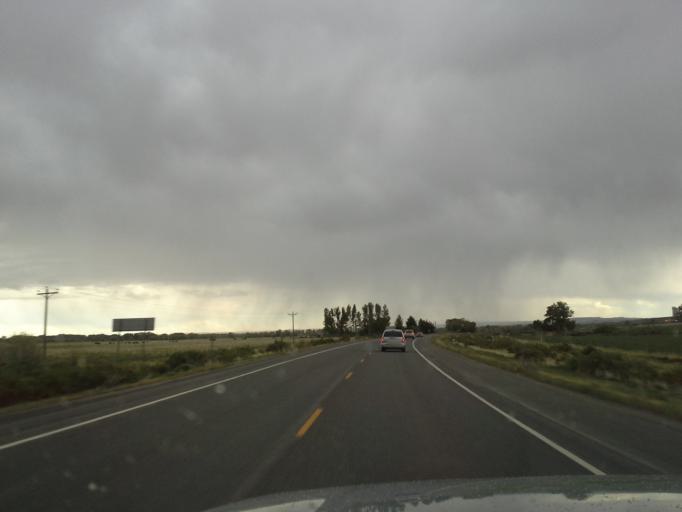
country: US
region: Wyoming
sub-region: Park County
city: Powell
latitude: 45.0064
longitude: -108.6233
